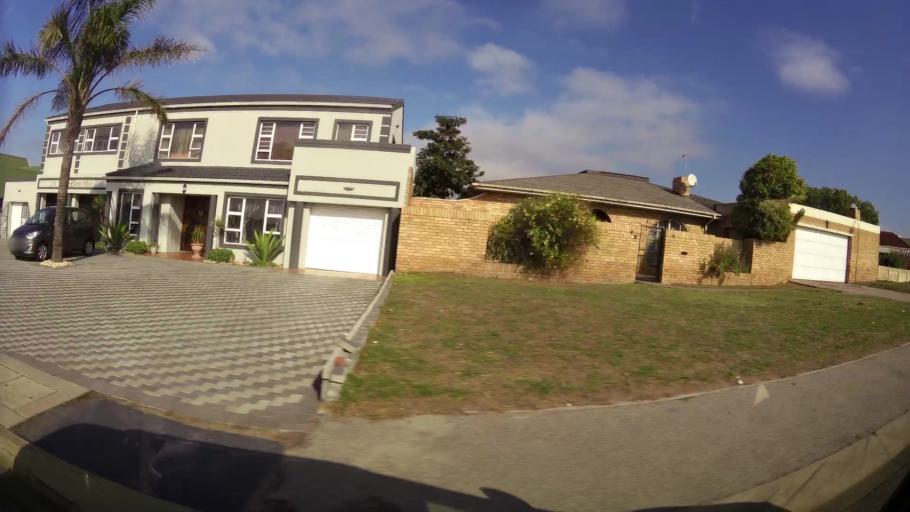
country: ZA
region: Eastern Cape
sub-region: Nelson Mandela Bay Metropolitan Municipality
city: Port Elizabeth
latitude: -33.9206
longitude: 25.5312
